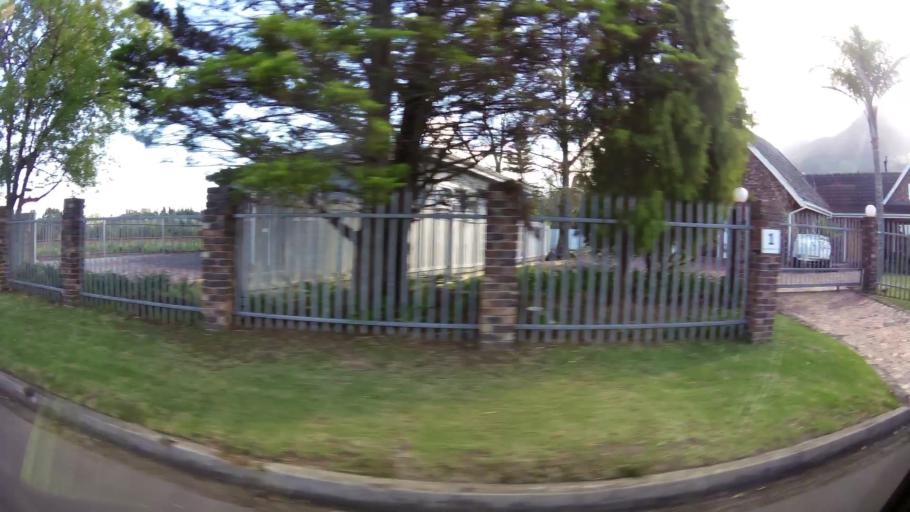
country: ZA
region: Western Cape
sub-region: Eden District Municipality
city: George
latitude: -33.9444
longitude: 22.4646
